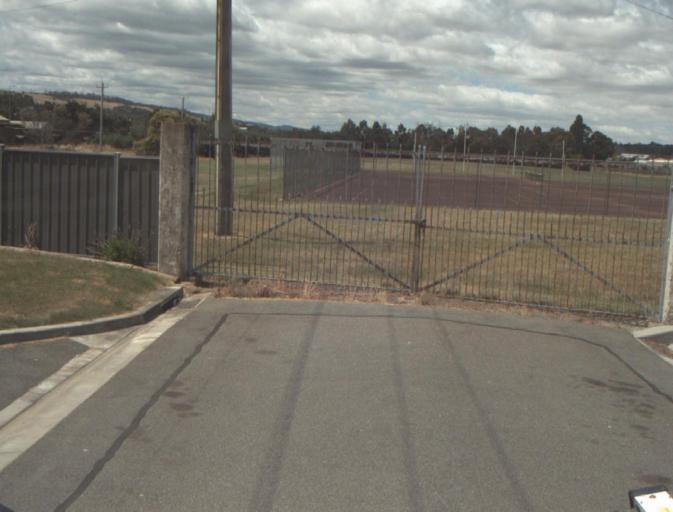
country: AU
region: Tasmania
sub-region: Launceston
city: Newstead
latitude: -41.4315
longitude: 147.1603
